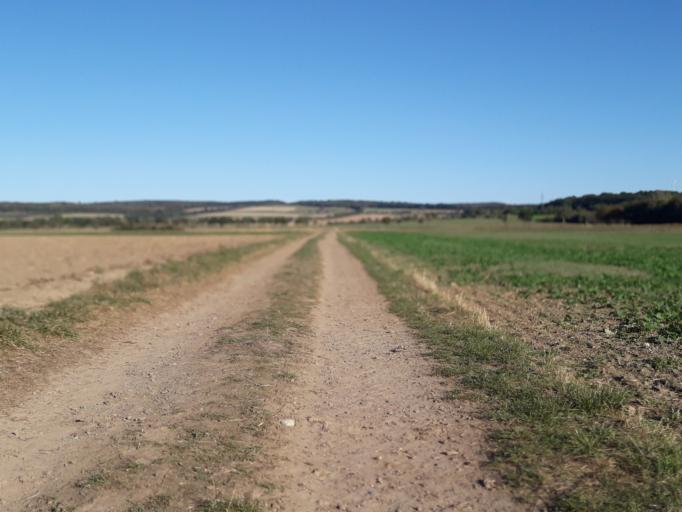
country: DE
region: North Rhine-Westphalia
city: Bad Lippspringe
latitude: 51.7629
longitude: 8.8279
